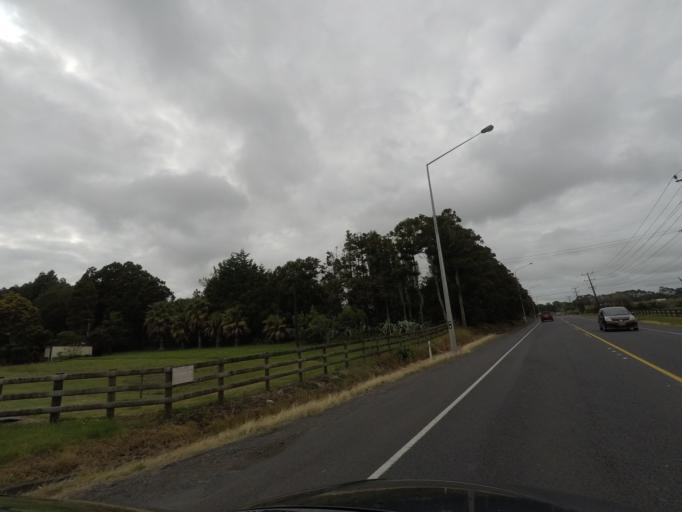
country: NZ
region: Auckland
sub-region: Auckland
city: Muriwai Beach
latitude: -36.7831
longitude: 174.5711
